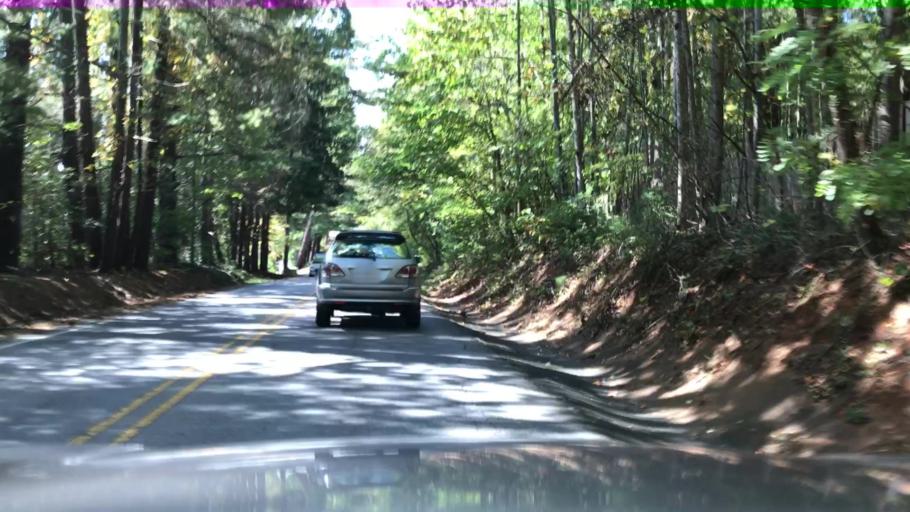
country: US
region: North Carolina
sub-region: Buncombe County
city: Royal Pines
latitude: 35.4951
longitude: -82.5335
